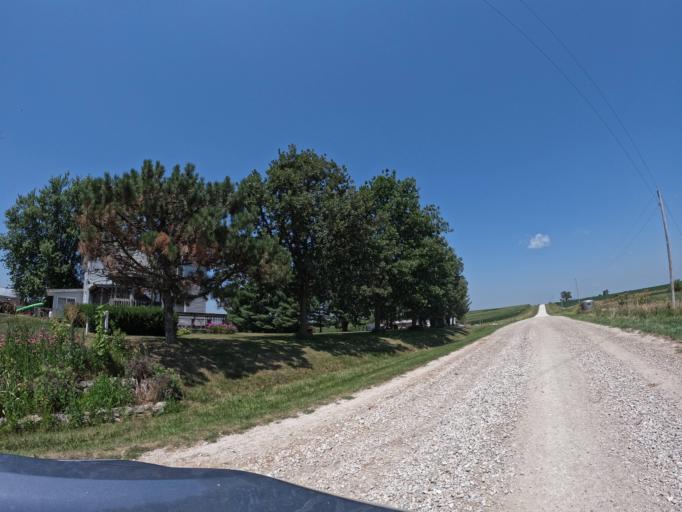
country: US
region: Iowa
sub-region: Keokuk County
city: Sigourney
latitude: 41.2608
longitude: -92.1697
